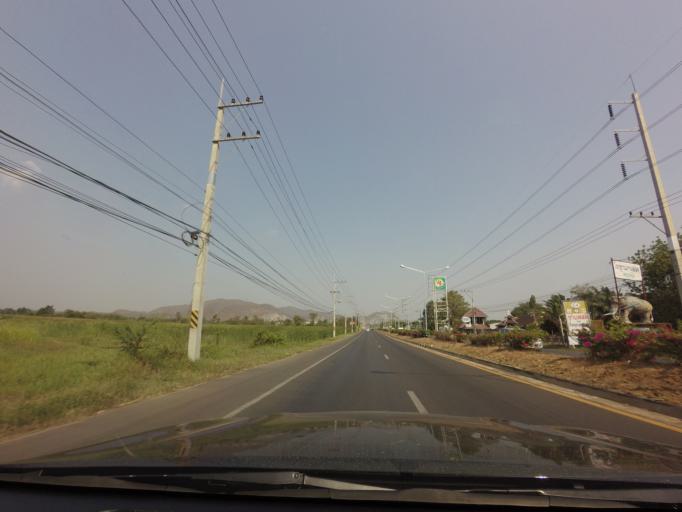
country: TH
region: Kanchanaburi
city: Kanchanaburi
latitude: 14.0598
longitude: 99.4732
